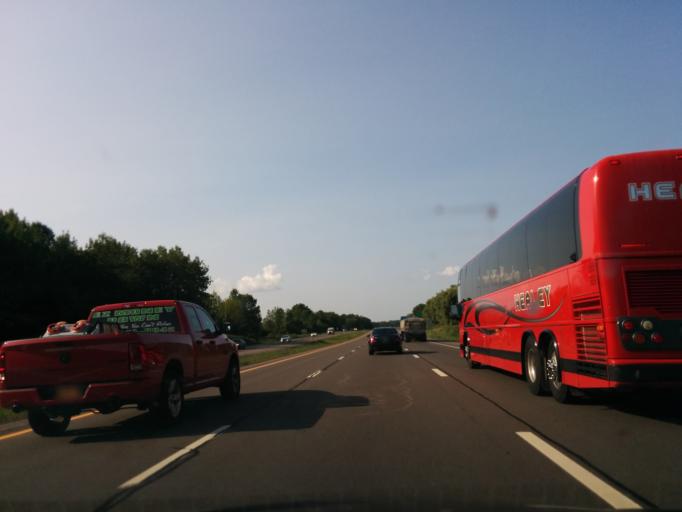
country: US
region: New York
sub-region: Onondaga County
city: North Syracuse
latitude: 43.1563
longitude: -76.1105
